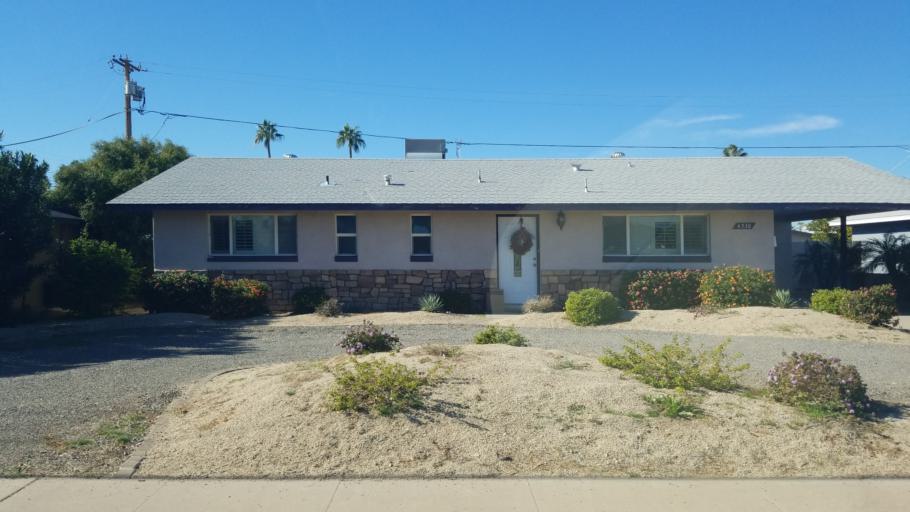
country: US
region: Arizona
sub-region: Maricopa County
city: Scottsdale
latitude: 33.5036
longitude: -111.9175
